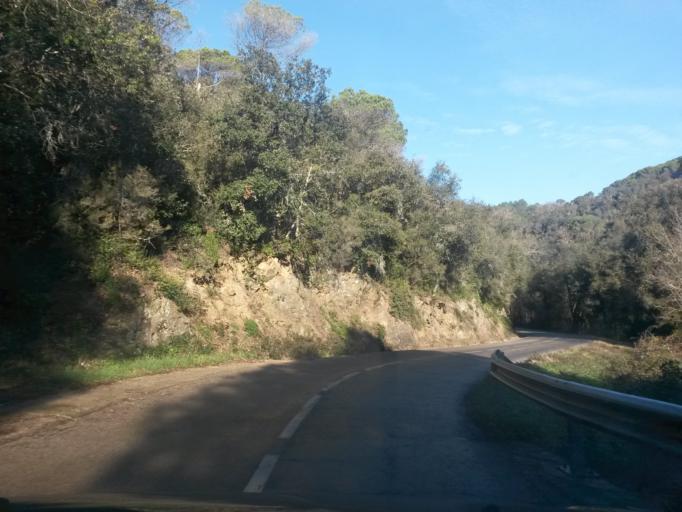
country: ES
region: Catalonia
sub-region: Provincia de Girona
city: Sant Gregori
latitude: 41.9846
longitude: 2.6867
